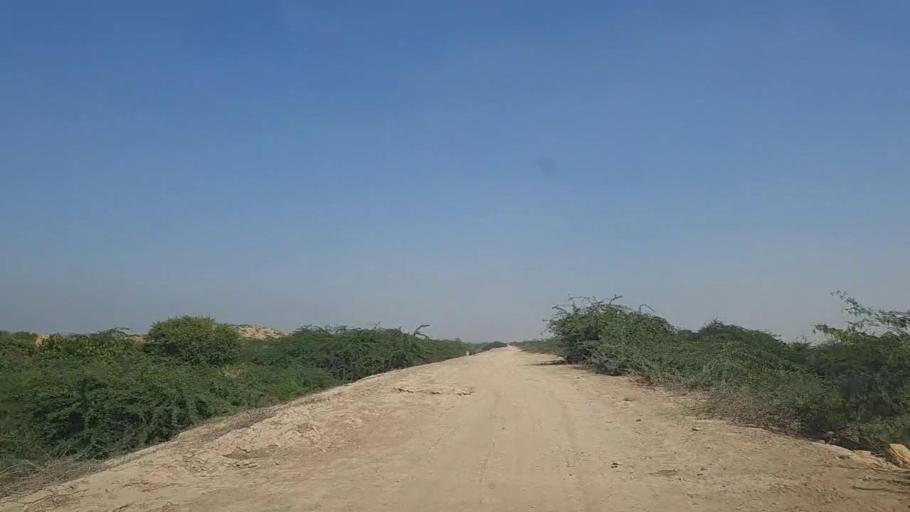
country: PK
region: Sindh
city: Daro Mehar
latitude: 24.8642
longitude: 68.0419
